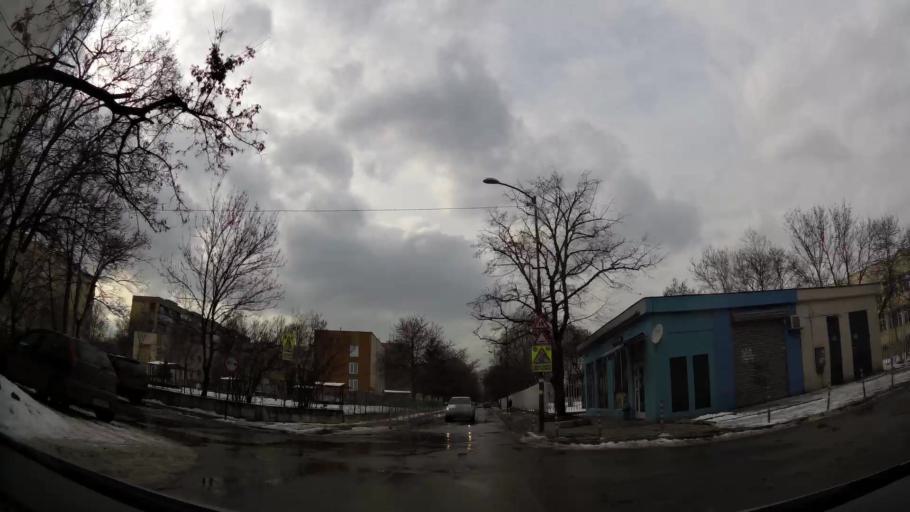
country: BG
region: Sofia-Capital
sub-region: Stolichna Obshtina
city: Sofia
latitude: 42.7005
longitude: 23.3640
